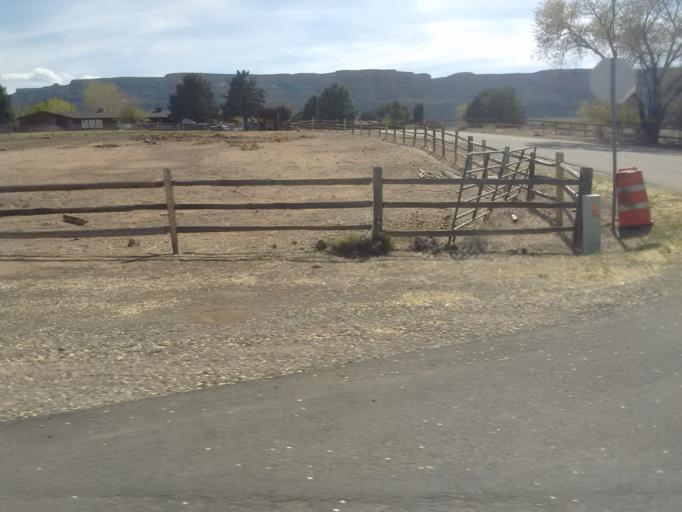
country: US
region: Colorado
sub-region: Mesa County
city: Redlands
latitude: 39.0876
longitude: -108.6529
